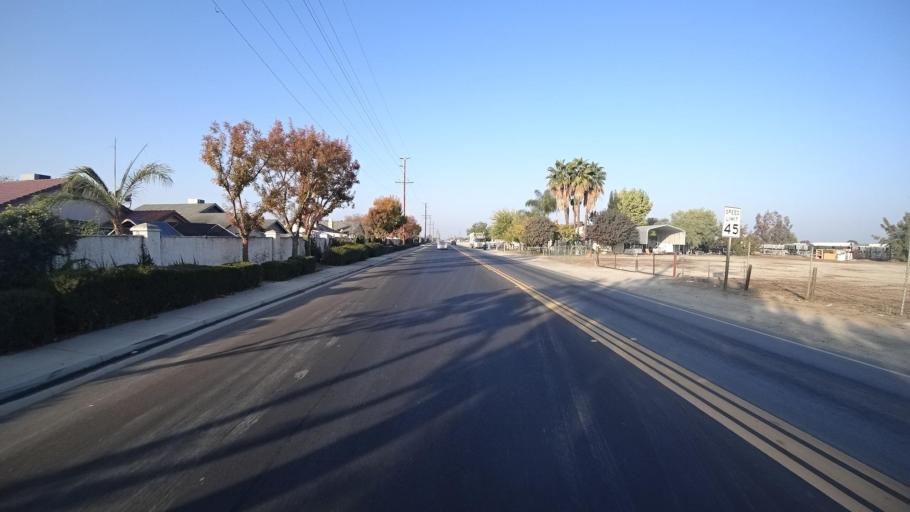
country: US
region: California
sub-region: Kern County
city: Delano
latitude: 35.7905
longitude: -119.2266
